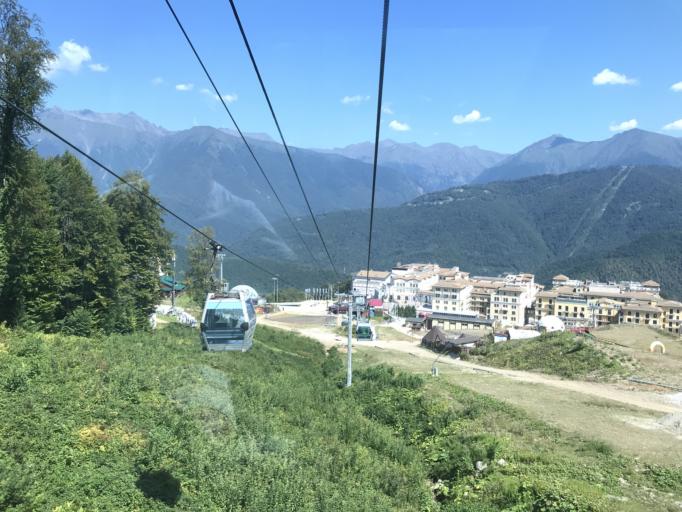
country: RU
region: Krasnodarskiy
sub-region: Sochi City
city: Krasnaya Polyana
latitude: 43.6662
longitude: 40.2569
